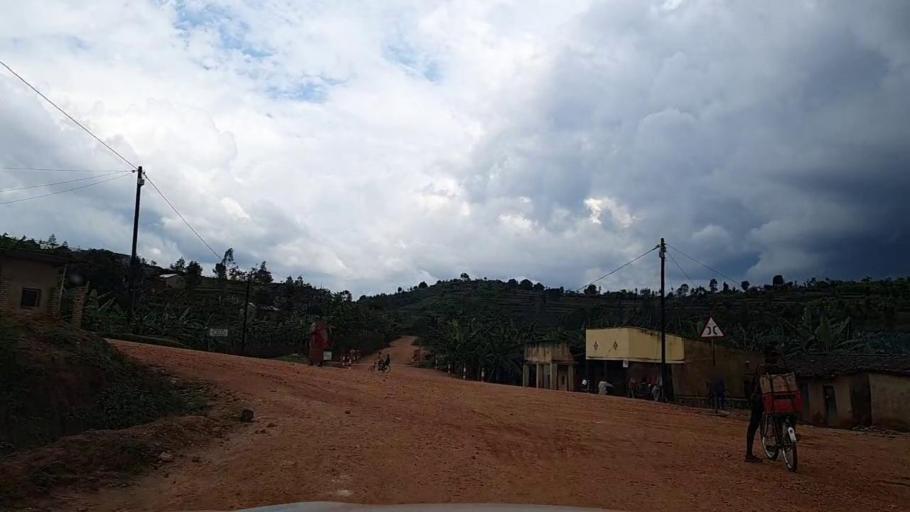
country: RW
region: Southern Province
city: Gikongoro
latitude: -2.4169
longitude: 29.6645
